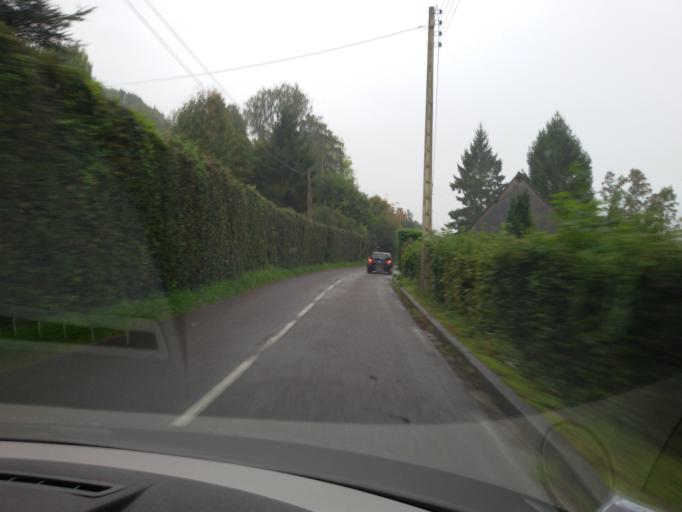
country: FR
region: Lower Normandy
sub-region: Departement du Calvados
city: Ablon
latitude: 49.4180
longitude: 0.3153
